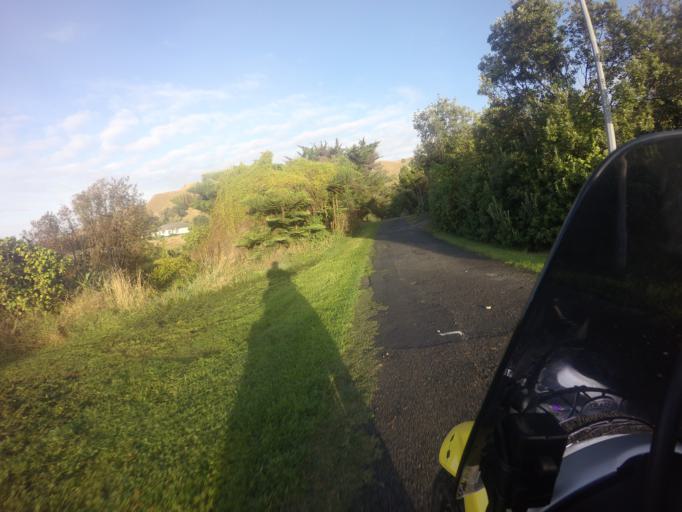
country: NZ
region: Gisborne
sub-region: Gisborne District
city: Gisborne
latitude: -38.6772
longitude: 178.0795
